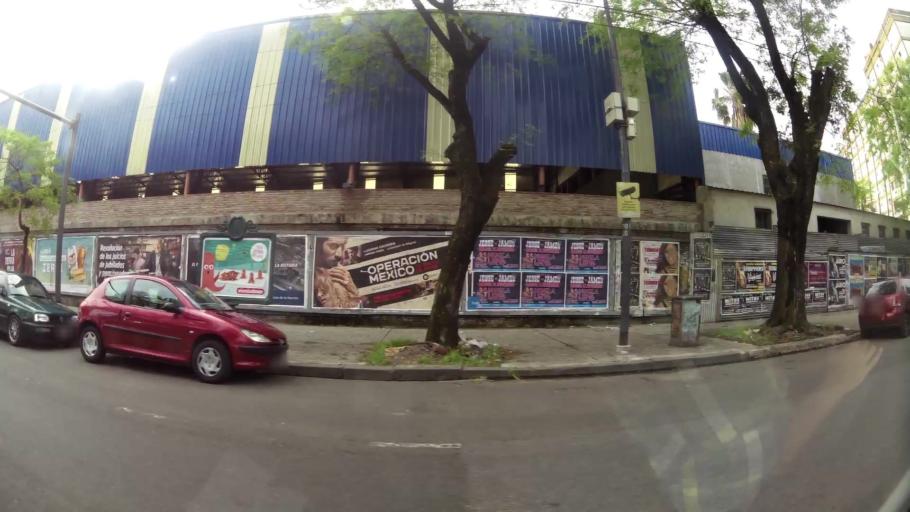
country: AR
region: Buenos Aires F.D.
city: Villa Santa Rita
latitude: -34.6427
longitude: -58.4817
